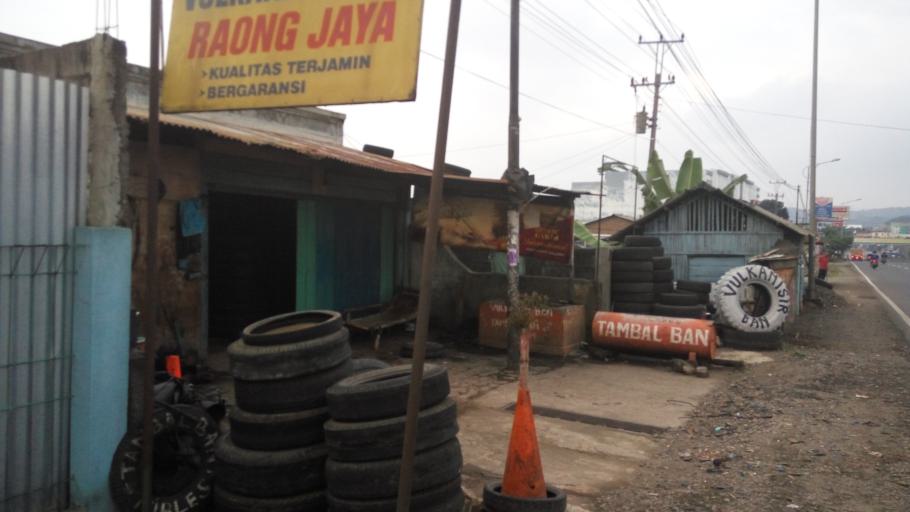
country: ID
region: Central Java
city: Ambarawa
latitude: -7.2280
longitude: 110.4306
